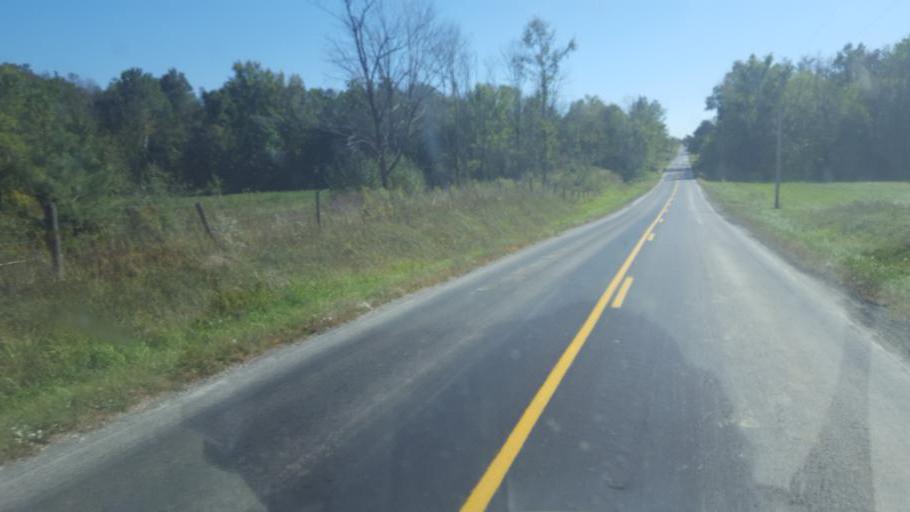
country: US
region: Ohio
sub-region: Wayne County
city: West Salem
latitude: 40.9478
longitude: -82.1620
